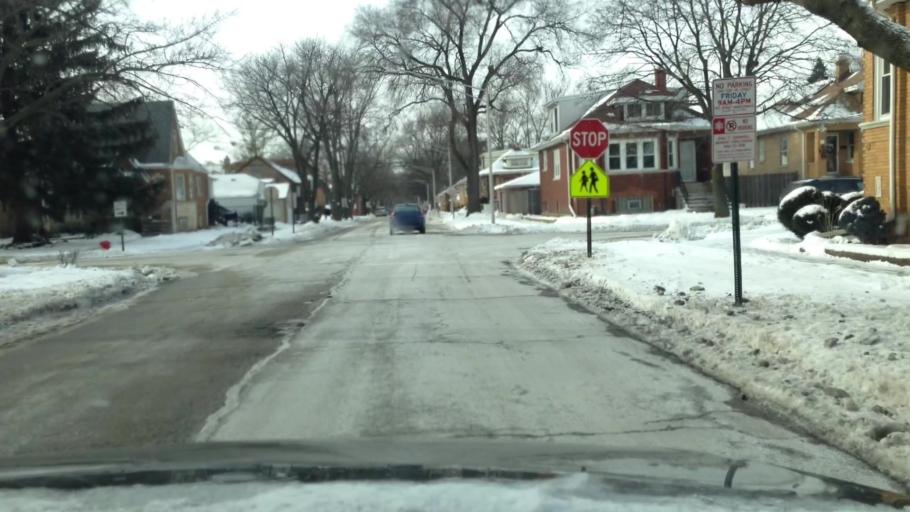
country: US
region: Illinois
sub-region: Cook County
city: Elmwood Park
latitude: 41.9361
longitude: -87.8185
